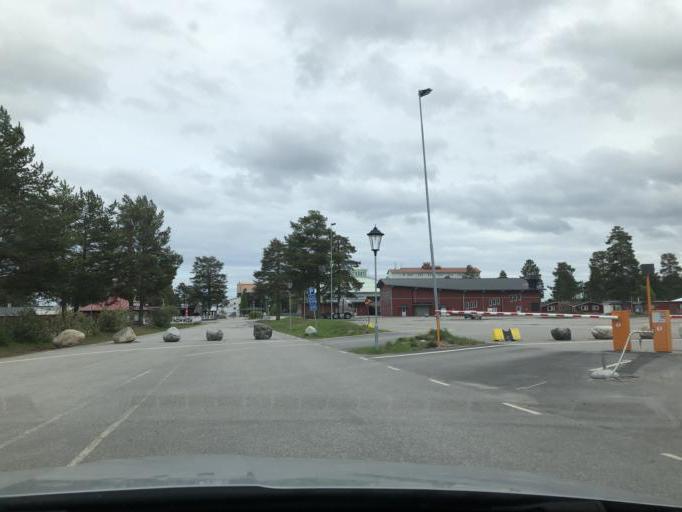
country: SE
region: Norrbotten
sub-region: Pitea Kommun
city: Pitea
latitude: 65.2359
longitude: 21.5303
